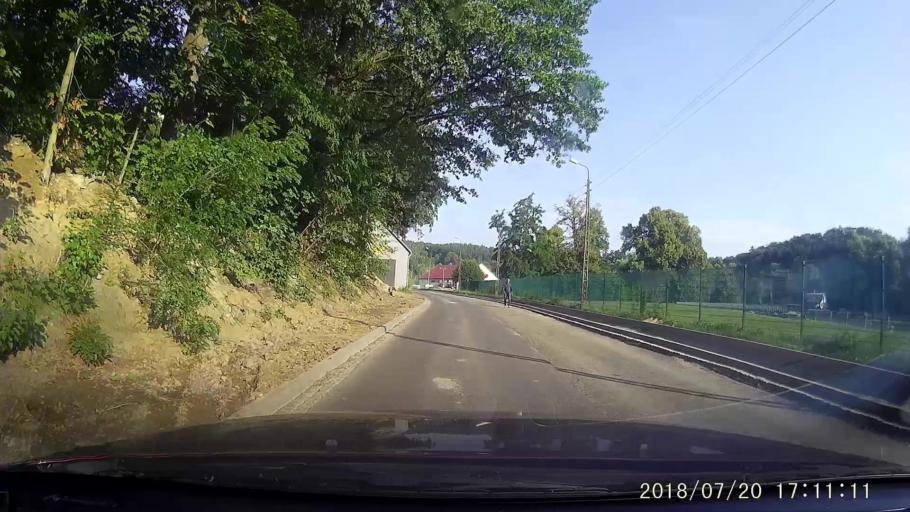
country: PL
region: Lower Silesian Voivodeship
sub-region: Powiat lubanski
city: Lesna
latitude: 51.0233
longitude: 15.2699
